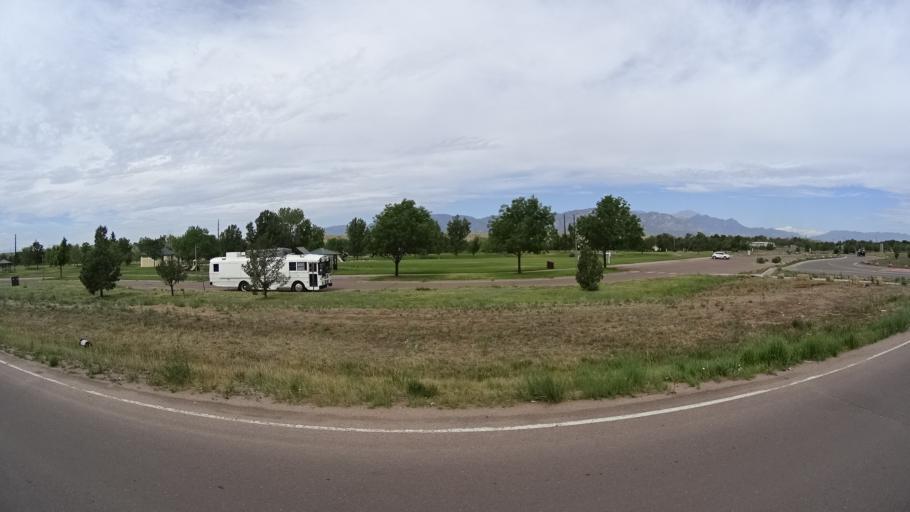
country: US
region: Colorado
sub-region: El Paso County
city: Fountain
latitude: 38.7086
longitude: -104.7115
